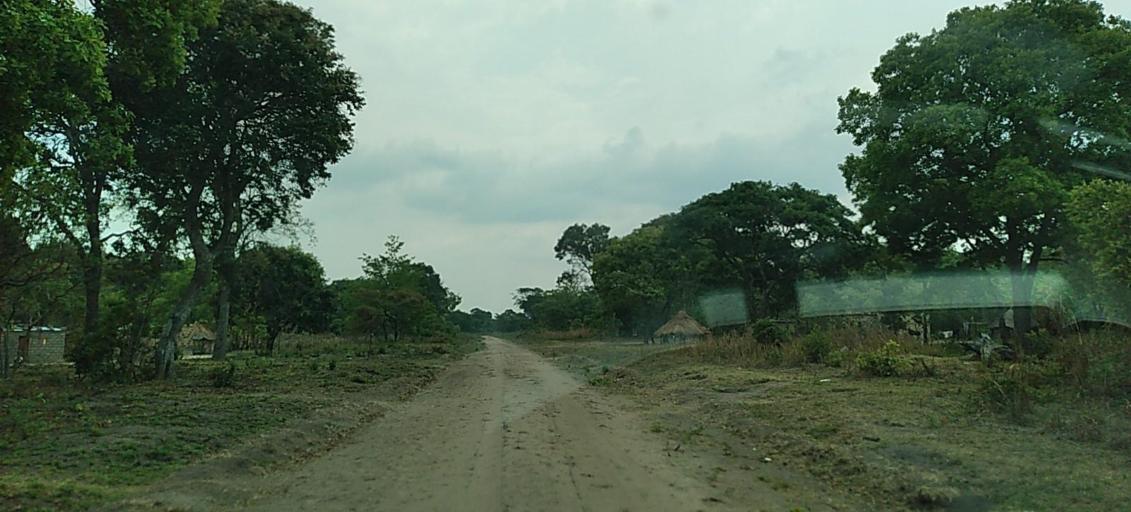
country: ZM
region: North-Western
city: Mwinilunga
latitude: -11.4051
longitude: 24.6305
